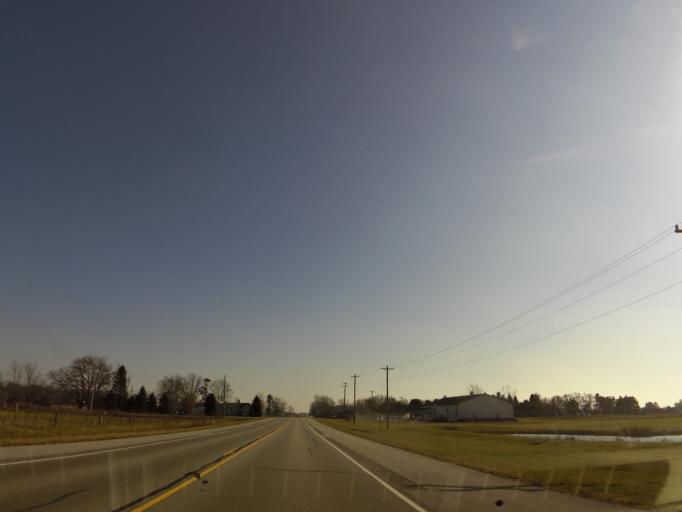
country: US
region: Indiana
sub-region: Union County
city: Liberty
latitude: 39.5914
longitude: -84.8543
